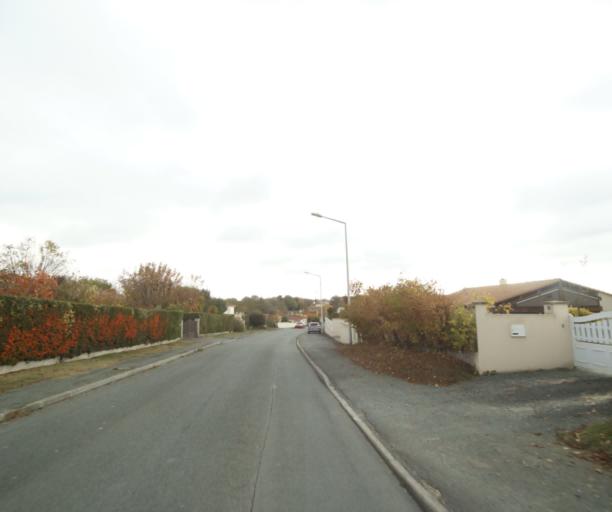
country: FR
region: Poitou-Charentes
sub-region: Departement de la Charente-Maritime
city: Saint-Georges-des-Coteaux
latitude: 45.7689
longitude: -0.7075
